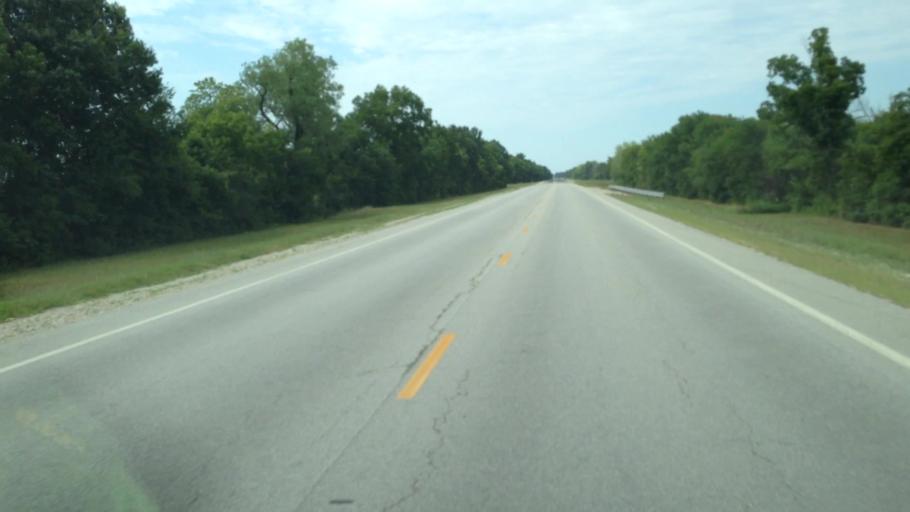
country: US
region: Kansas
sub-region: Labette County
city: Chetopa
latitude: 37.0591
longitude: -95.1027
